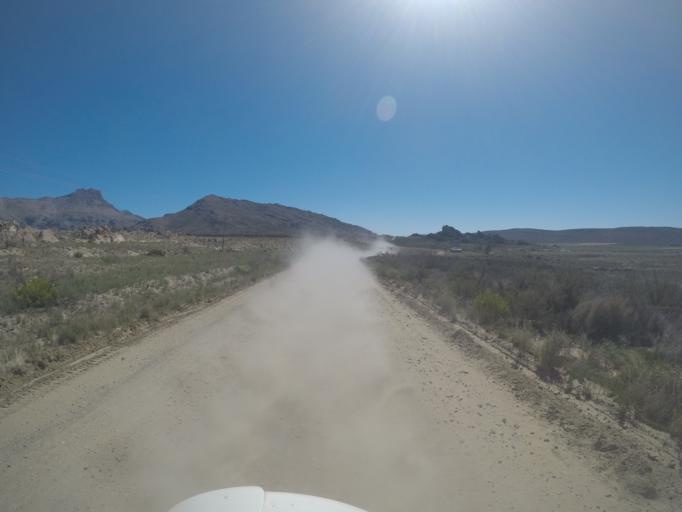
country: ZA
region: Western Cape
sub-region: Cape Winelands District Municipality
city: Ceres
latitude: -32.8623
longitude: 19.4433
